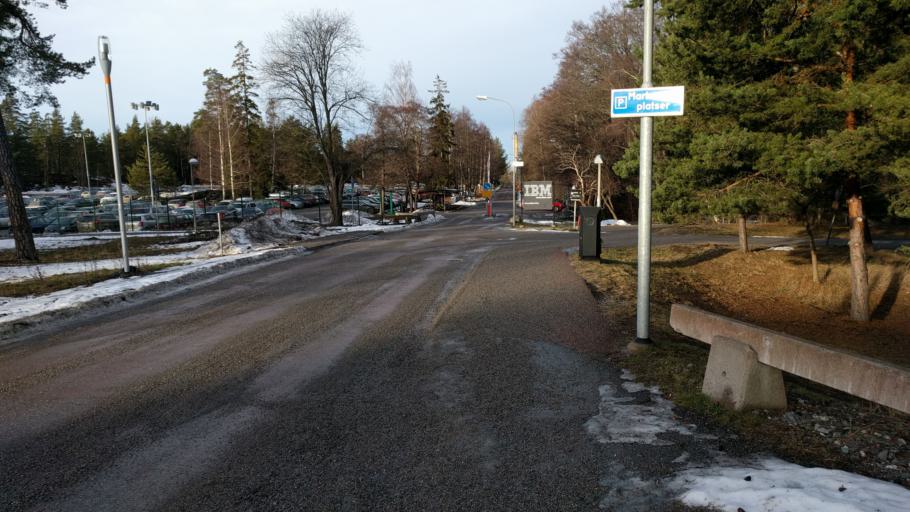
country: SE
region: Stockholm
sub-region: Stockholms Kommun
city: Kista
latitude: 59.4098
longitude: 17.9386
